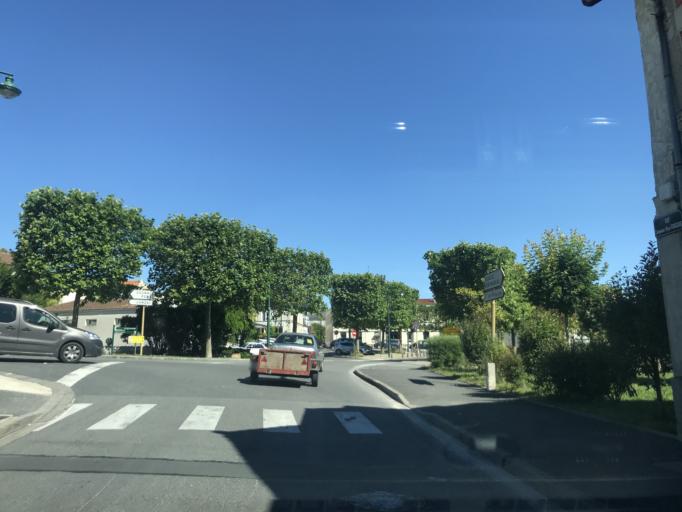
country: FR
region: Poitou-Charentes
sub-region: Departement de la Charente
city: Barbezieux-Saint-Hilaire
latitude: 45.4703
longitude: -0.1524
